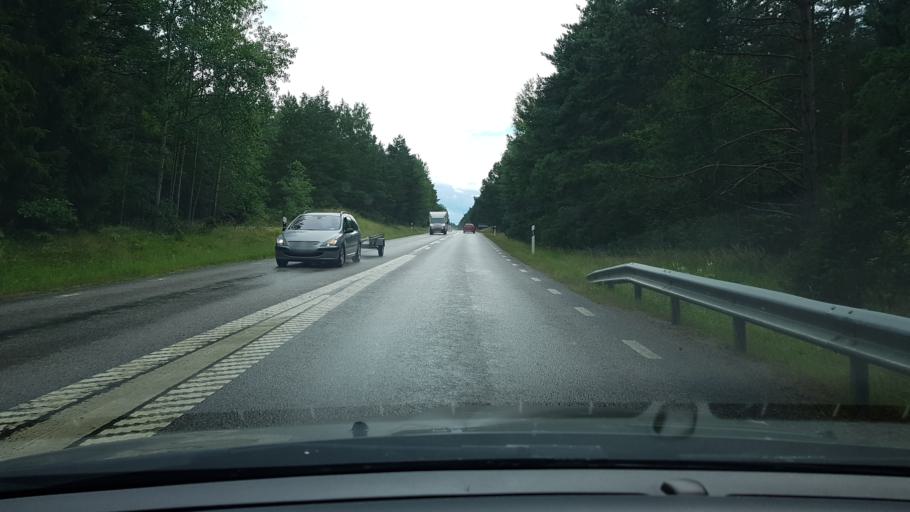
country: SE
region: Uppsala
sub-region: Uppsala Kommun
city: Saevja
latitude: 59.8072
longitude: 17.6879
